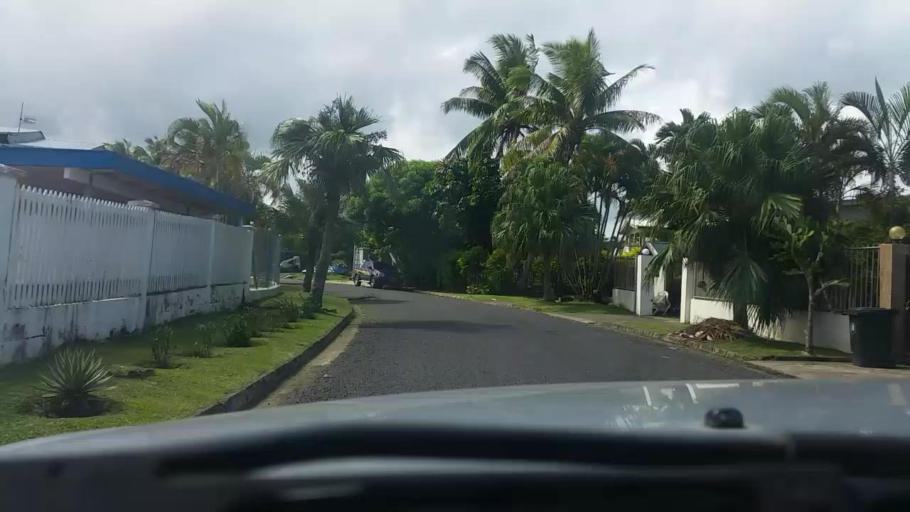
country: FJ
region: Central
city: Suva
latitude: -18.1325
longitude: 178.4661
